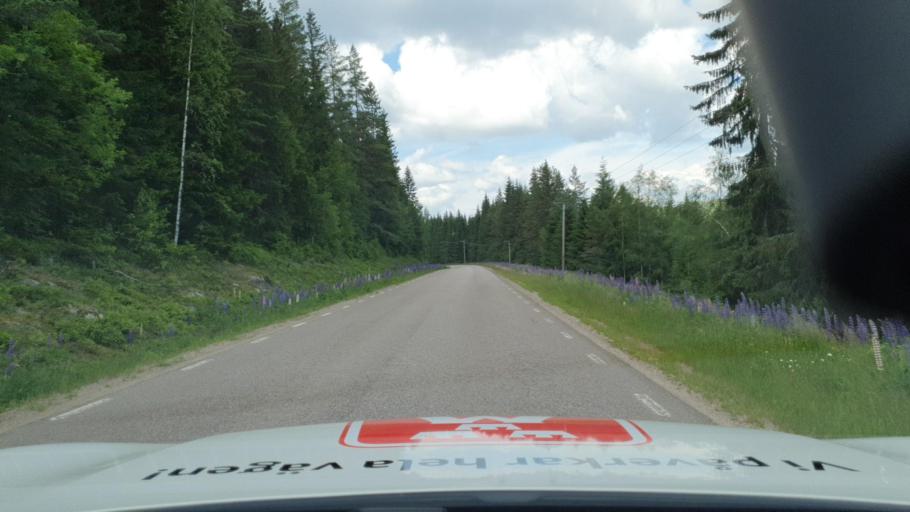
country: SE
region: Vaermland
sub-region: Torsby Kommun
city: Torsby
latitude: 60.4877
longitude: 12.8739
